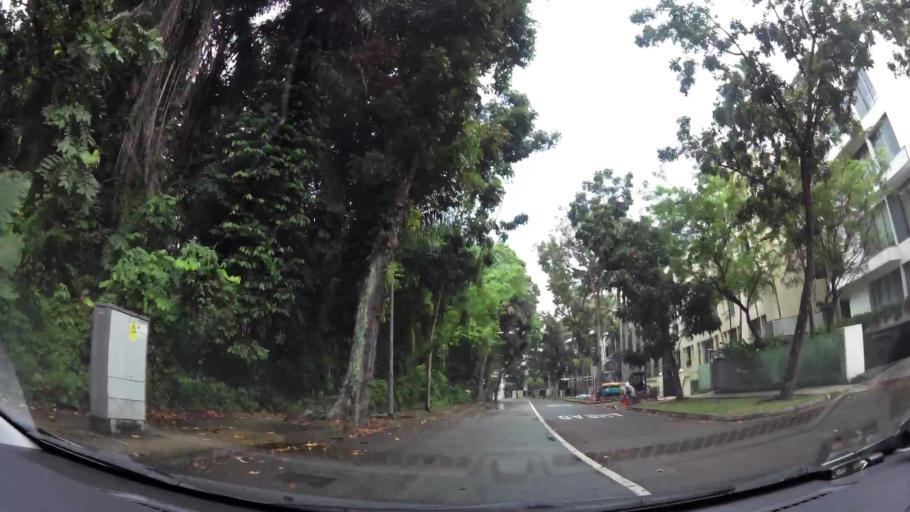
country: SG
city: Singapore
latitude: 1.3078
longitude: 103.8255
